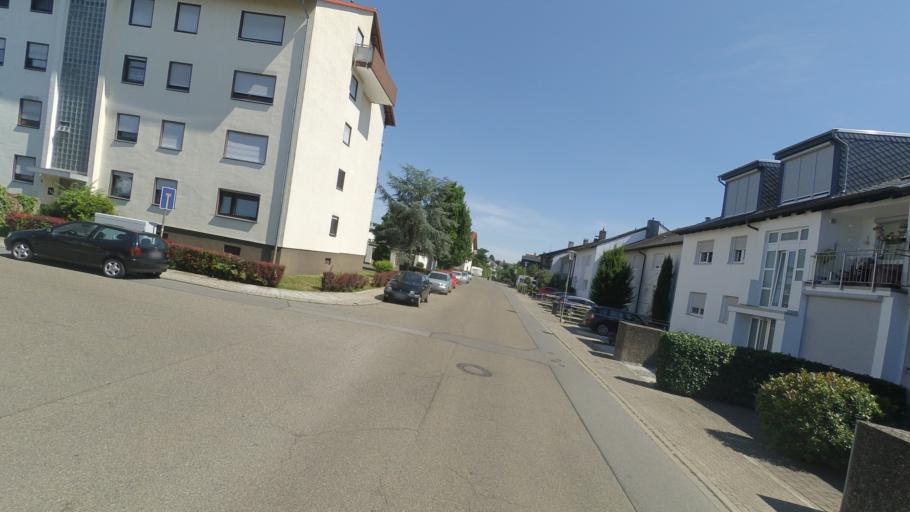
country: DE
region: Baden-Wuerttemberg
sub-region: Karlsruhe Region
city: Schwetzingen
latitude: 49.3926
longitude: 8.5589
